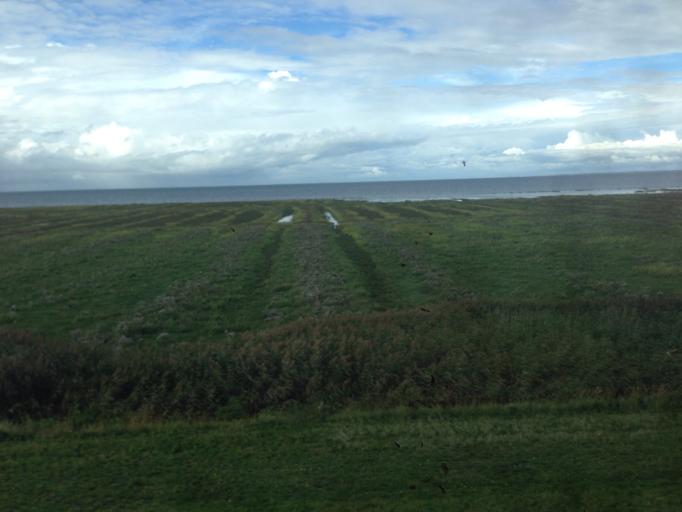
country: DE
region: Schleswig-Holstein
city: Friedrich-Wilhelm-Lubke-Koog
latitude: 54.8853
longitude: 8.5730
